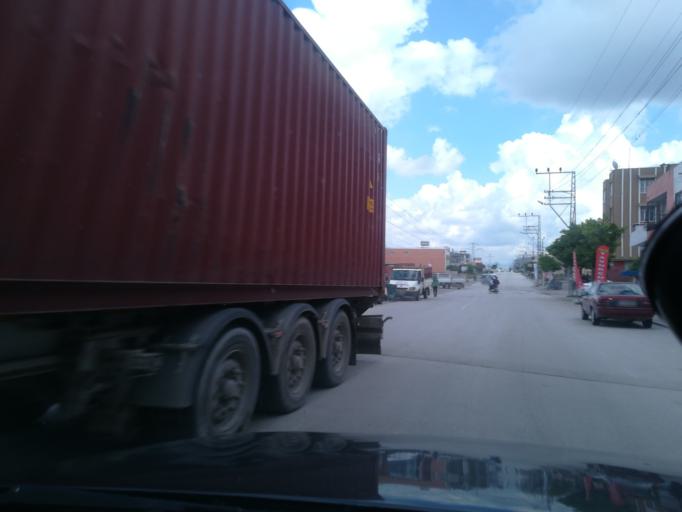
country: TR
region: Adana
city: Yuregir
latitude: 36.9761
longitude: 35.3888
